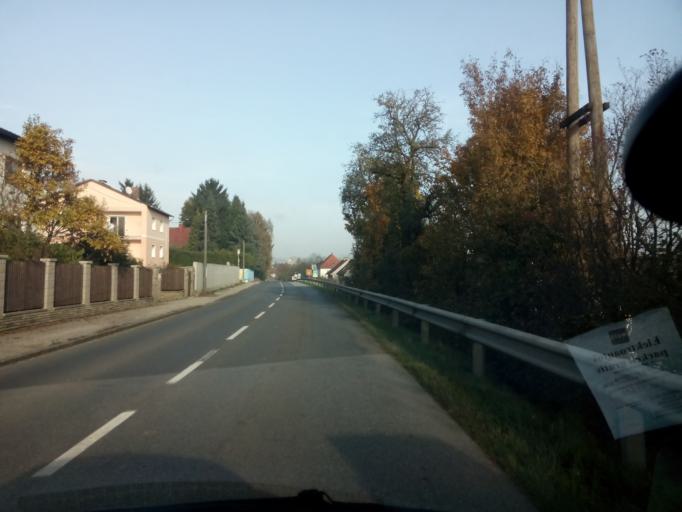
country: AT
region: Upper Austria
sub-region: Politischer Bezirk Steyr-Land
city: Bad Hall
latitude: 48.1319
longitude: 14.2233
